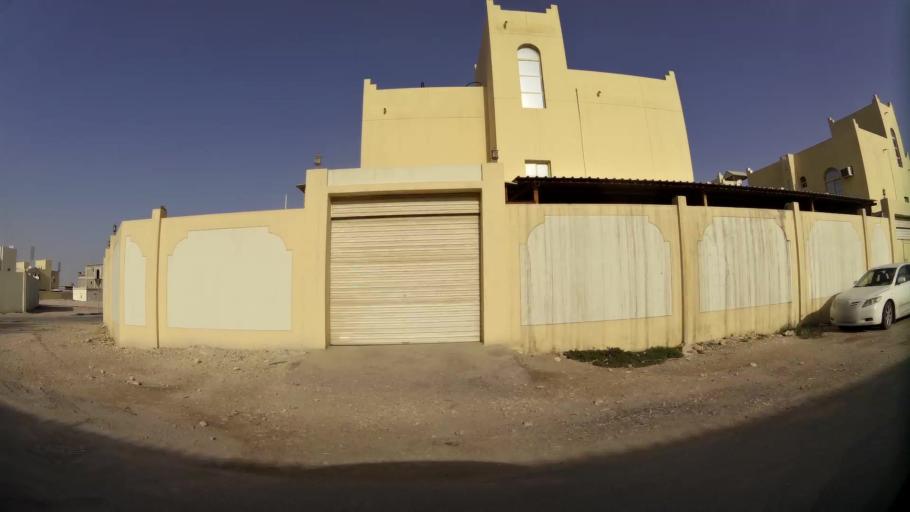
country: QA
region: Baladiyat ar Rayyan
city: Ar Rayyan
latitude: 25.3391
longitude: 51.4366
